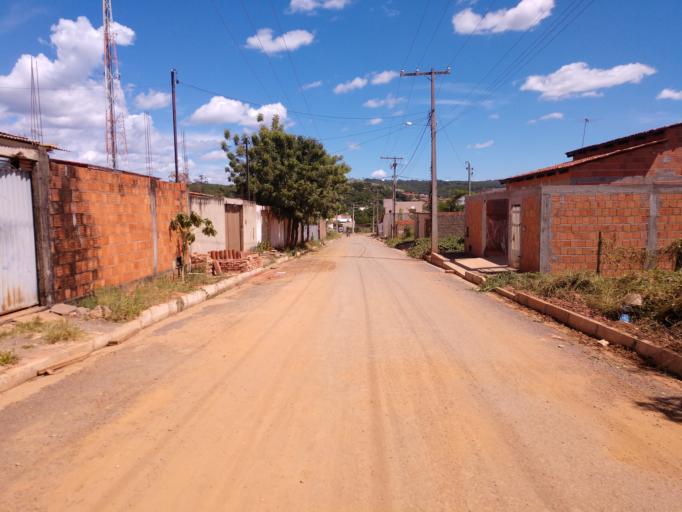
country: BR
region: Bahia
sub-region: Sao Desiderio
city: Sao Desiderio
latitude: -12.3574
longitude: -44.9724
